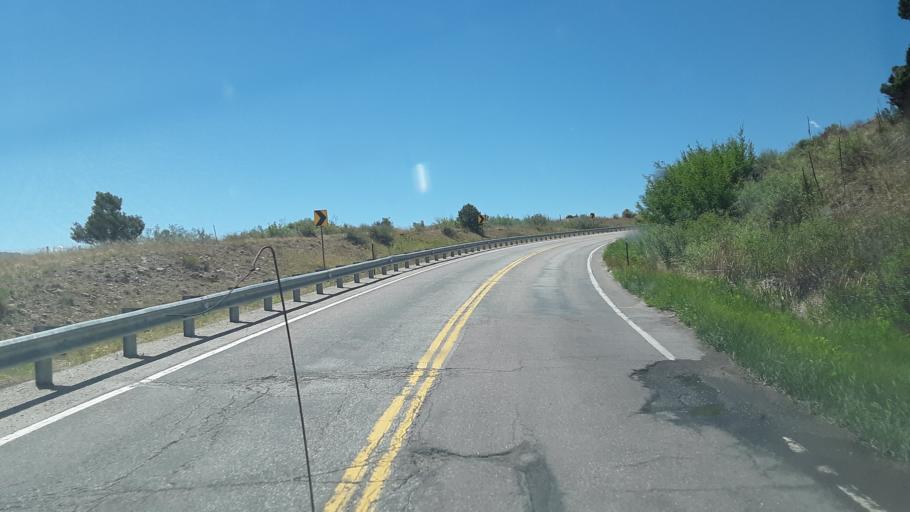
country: US
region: Colorado
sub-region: Custer County
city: Westcliffe
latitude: 38.2862
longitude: -105.6160
